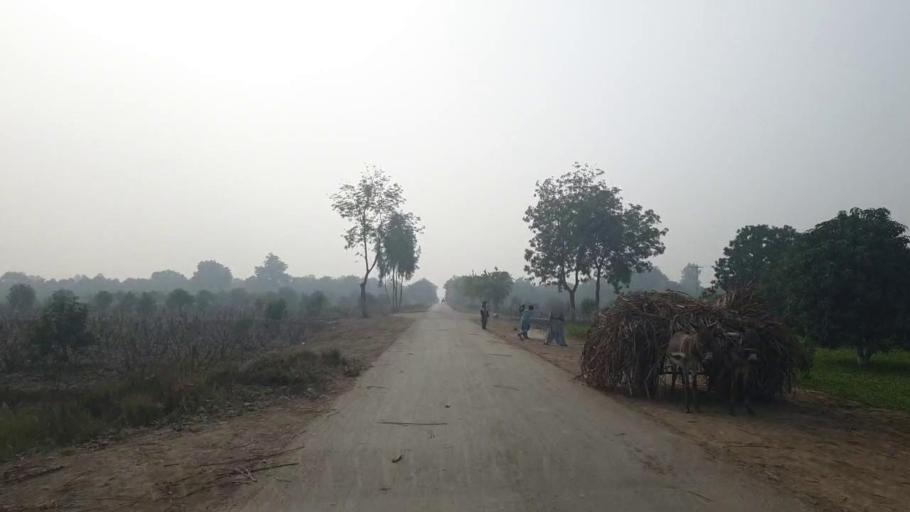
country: PK
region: Sindh
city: Tando Adam
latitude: 25.7845
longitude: 68.6073
